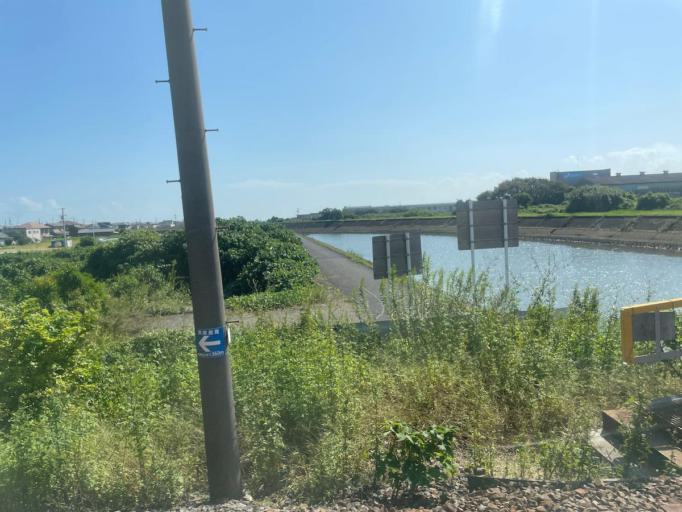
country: JP
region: Mie
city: Kawage
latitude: 34.8081
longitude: 136.5649
